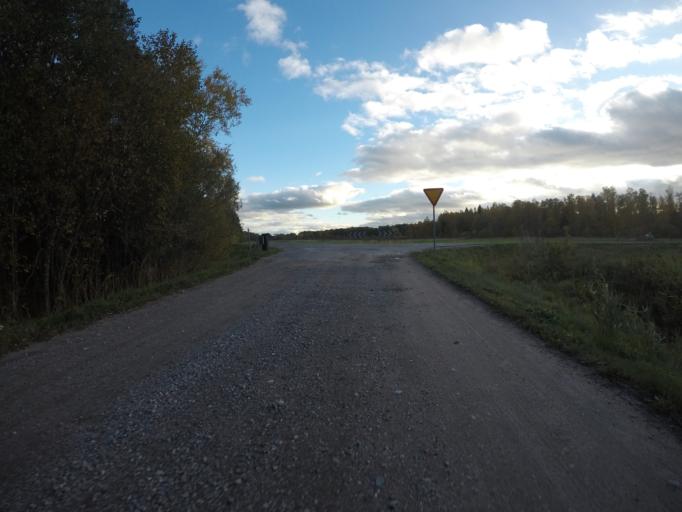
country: SE
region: Vaestmanland
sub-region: Arboga Kommun
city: Tyringe
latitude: 59.3149
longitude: 15.9799
